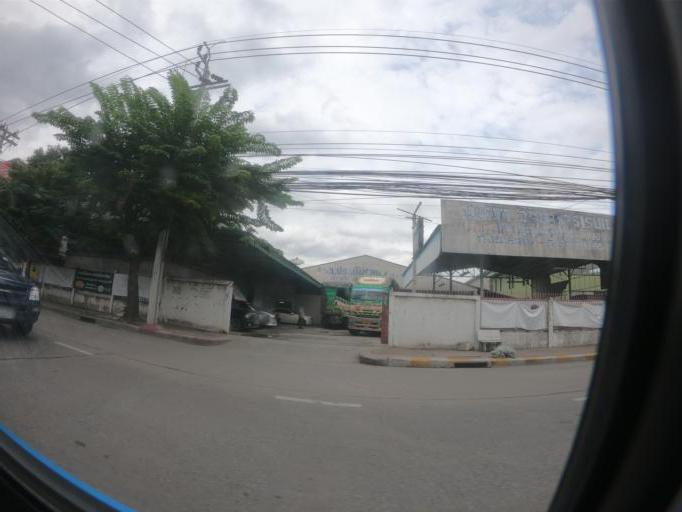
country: TH
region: Bangkok
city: Suan Luang
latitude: 13.7233
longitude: 100.6585
